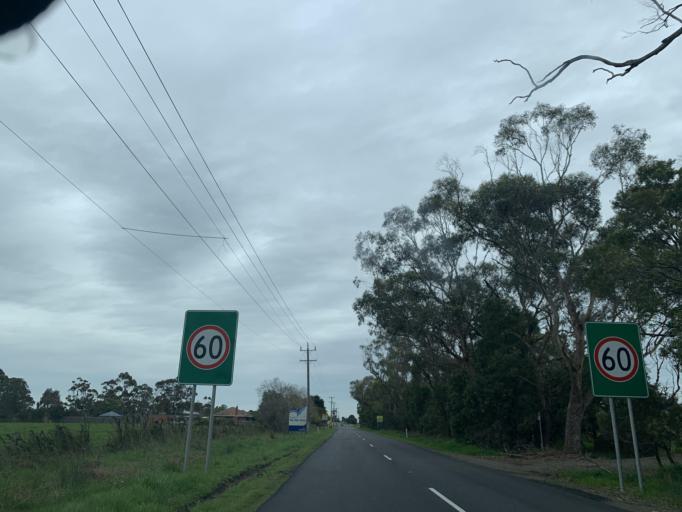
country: AU
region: Victoria
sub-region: Cardinia
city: Pakenham South
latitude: -38.0822
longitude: 145.5769
